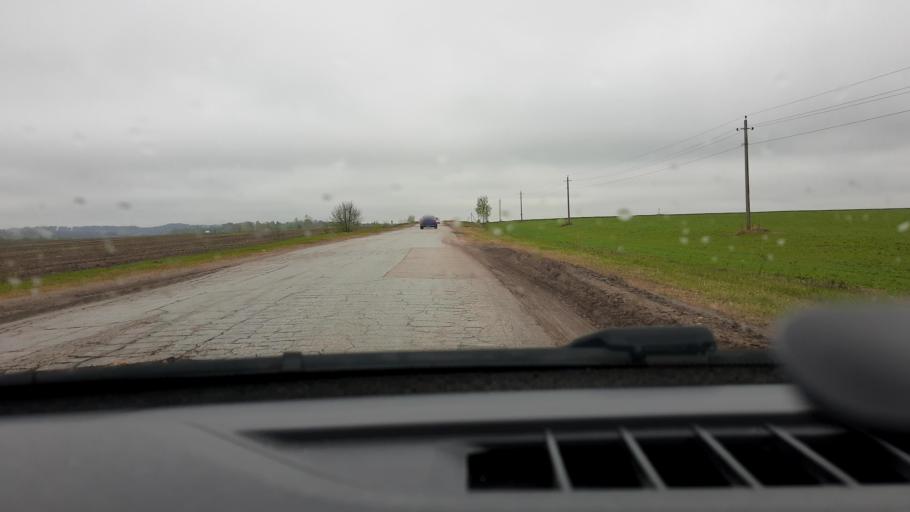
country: RU
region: Nizjnij Novgorod
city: Dal'neye Konstantinovo
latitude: 55.7647
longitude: 44.2457
